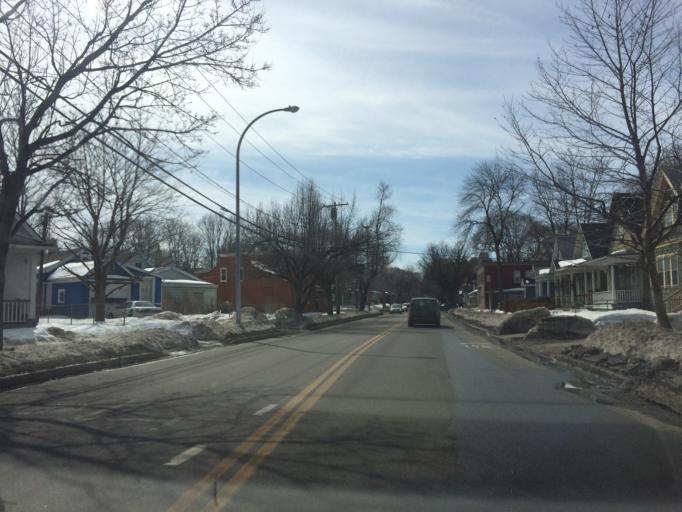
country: US
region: New York
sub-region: Monroe County
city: Rochester
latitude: 43.1391
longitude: -77.5964
